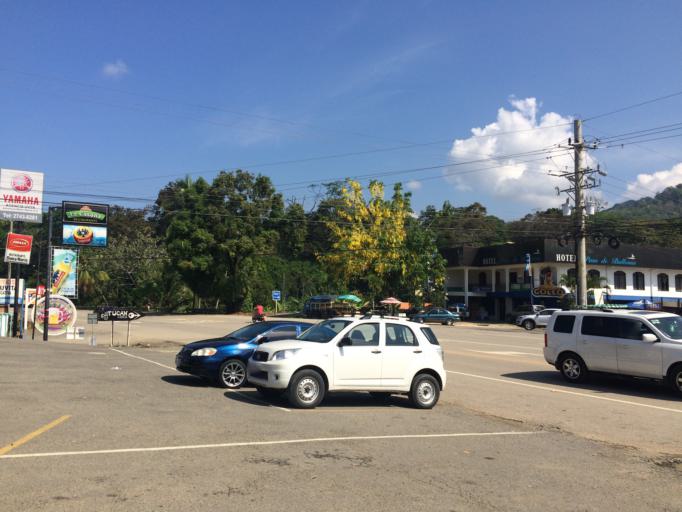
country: CR
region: San Jose
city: Daniel Flores
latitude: 9.1717
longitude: -83.7393
